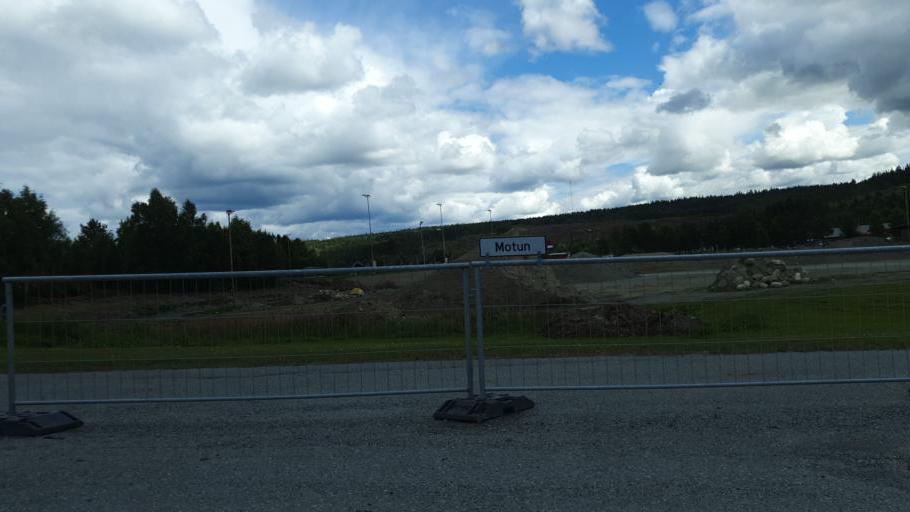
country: NO
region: Sor-Trondelag
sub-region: Rennebu
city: Berkak
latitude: 62.8303
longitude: 10.0043
